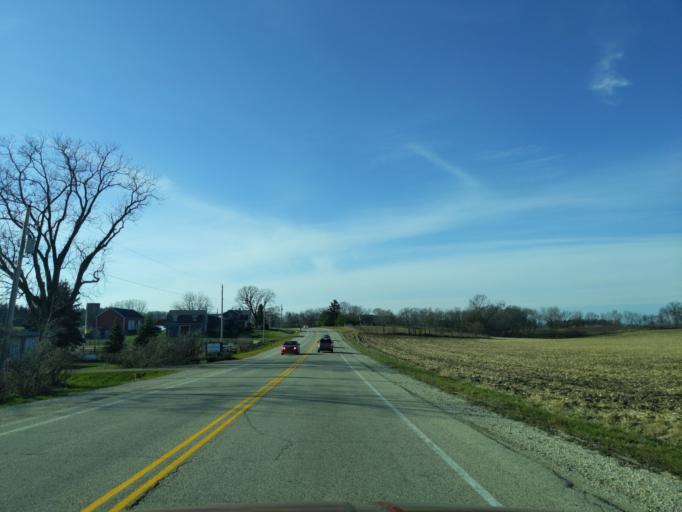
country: US
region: Wisconsin
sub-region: Rock County
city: Milton
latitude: 42.8244
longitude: -88.9056
